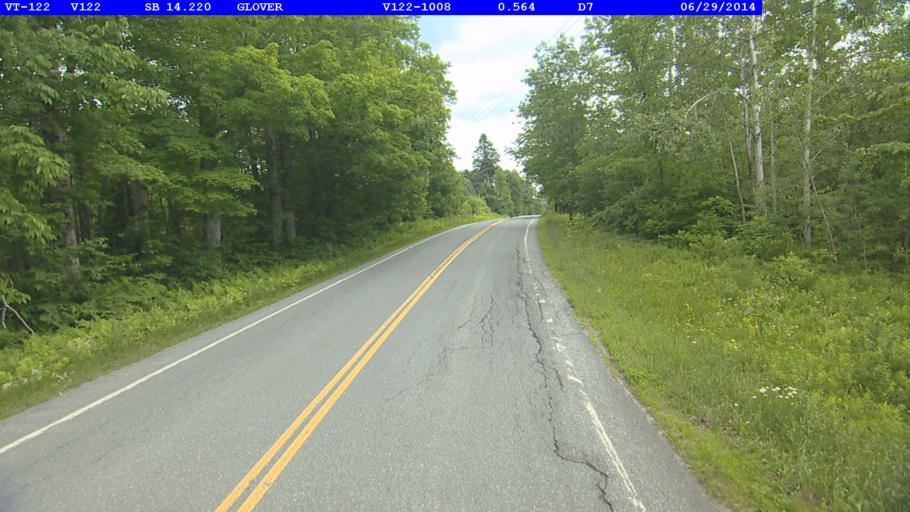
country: US
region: Vermont
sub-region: Caledonia County
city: Lyndonville
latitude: 44.6829
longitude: -72.1734
